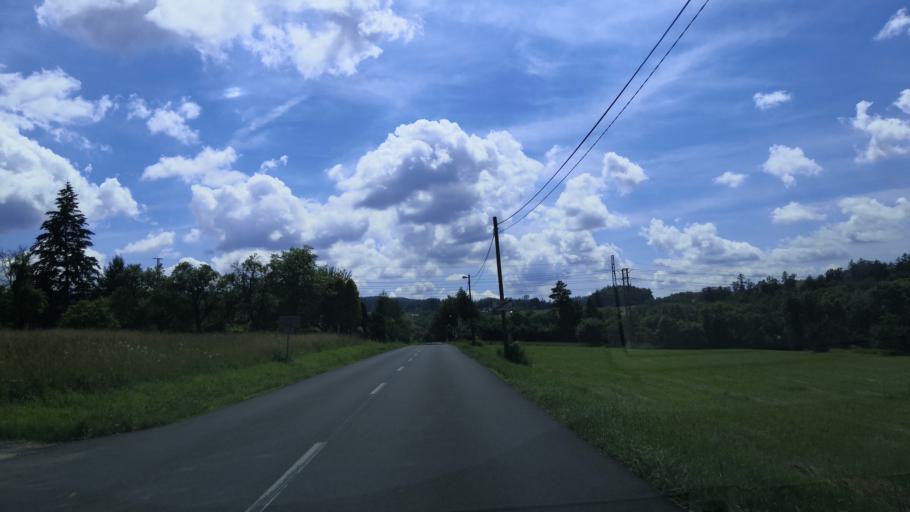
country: CZ
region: Zlin
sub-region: Okres Vsetin
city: Roznov pod Radhostem
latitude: 49.4499
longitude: 18.1408
